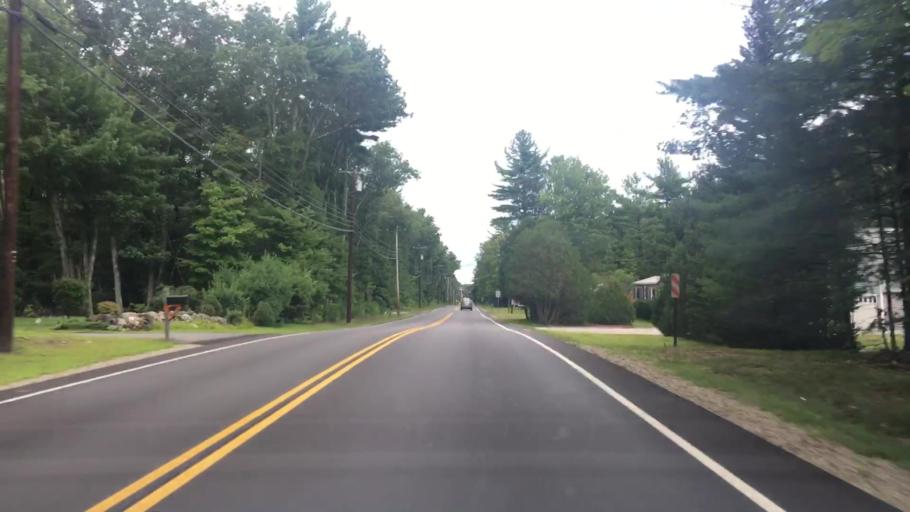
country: US
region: Maine
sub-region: York County
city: Dayton
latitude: 43.4972
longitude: -70.5915
